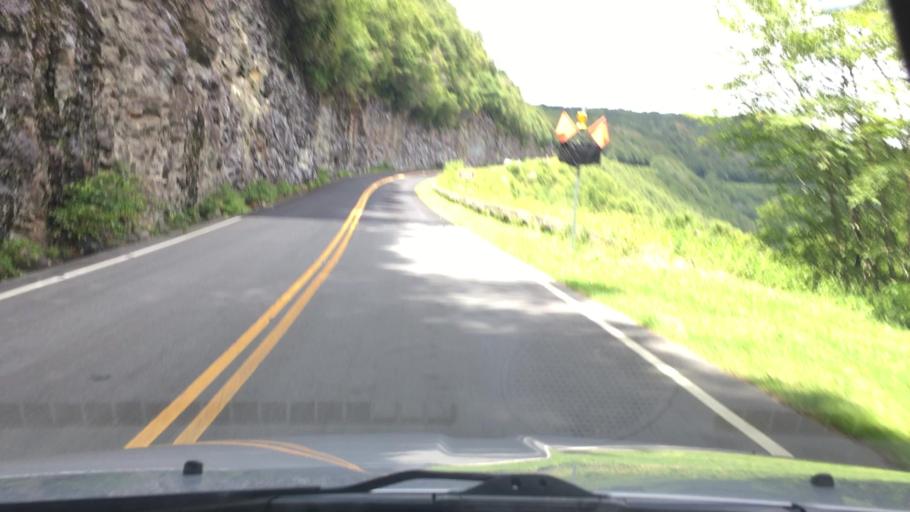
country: US
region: North Carolina
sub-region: Buncombe County
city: Swannanoa
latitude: 35.6878
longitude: -82.3837
